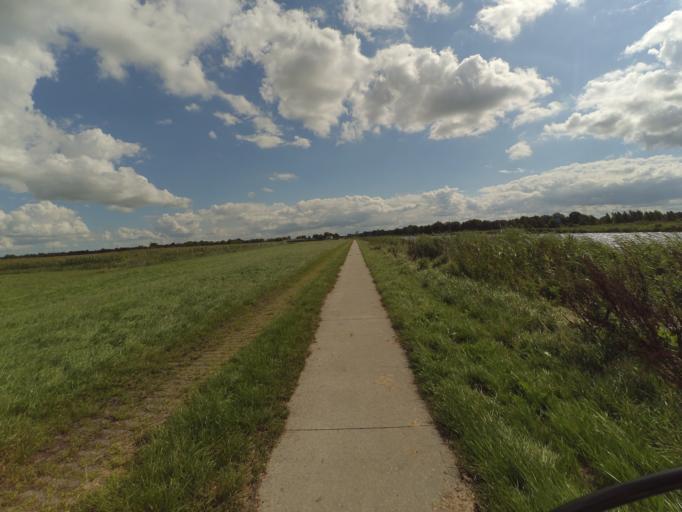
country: NL
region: Friesland
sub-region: Gemeente Tytsjerksteradiel
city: Eastermar
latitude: 53.1999
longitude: 6.0581
